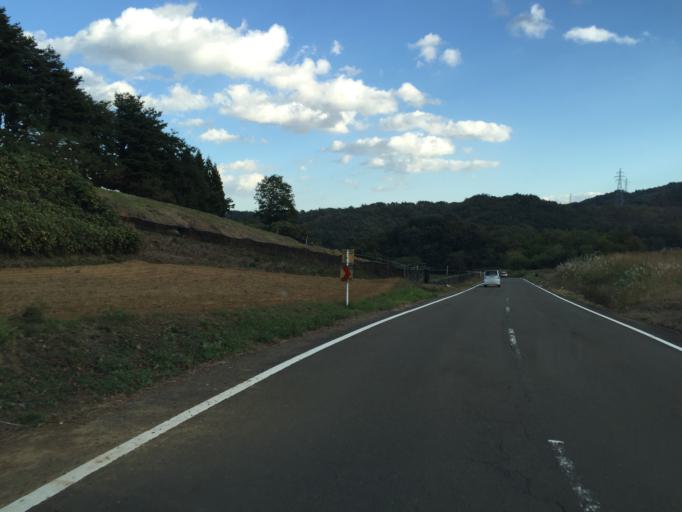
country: JP
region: Fukushima
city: Fukushima-shi
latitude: 37.7013
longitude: 140.3848
